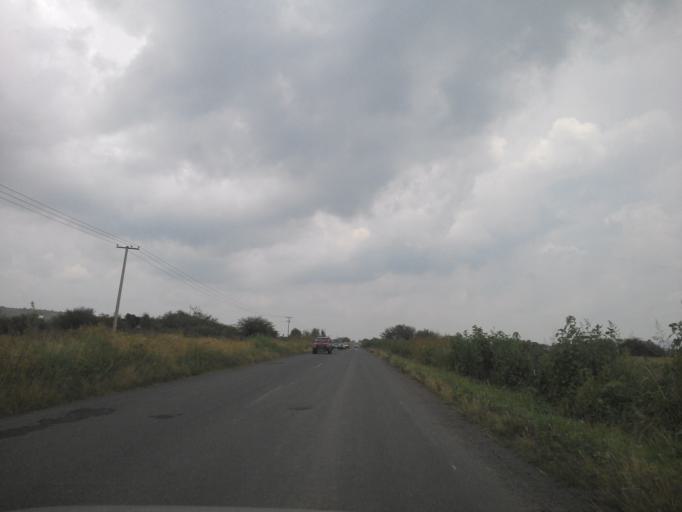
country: MX
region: Guanajuato
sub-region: San Francisco del Rincon
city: San Ignacio de Hidalgo
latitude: 20.8921
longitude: -101.9561
